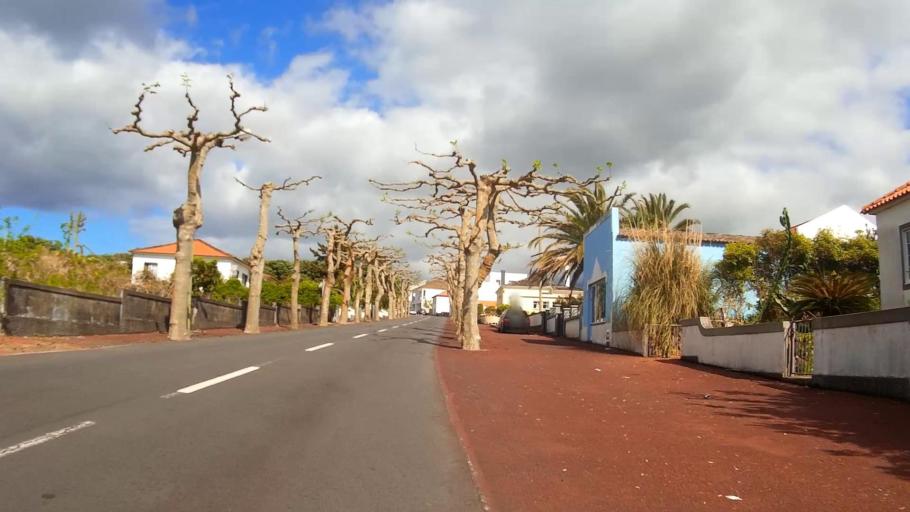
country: PT
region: Azores
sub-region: Madalena
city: Madalena
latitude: 38.5350
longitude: -28.5244
